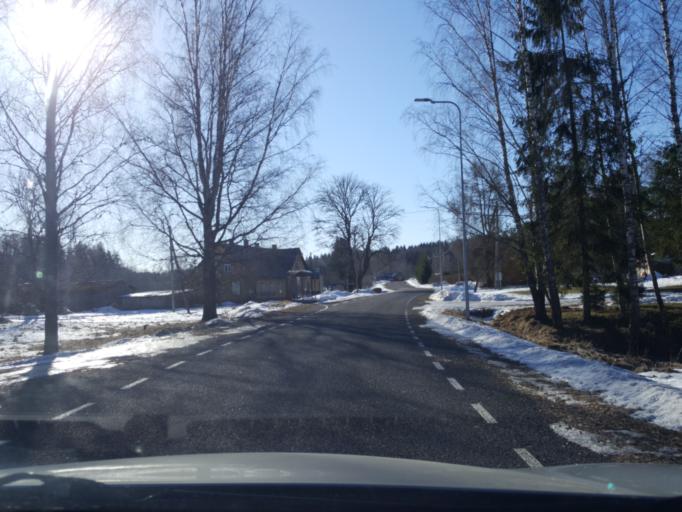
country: EE
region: Viljandimaa
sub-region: Vohma linn
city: Vohma
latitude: 58.5196
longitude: 25.6259
